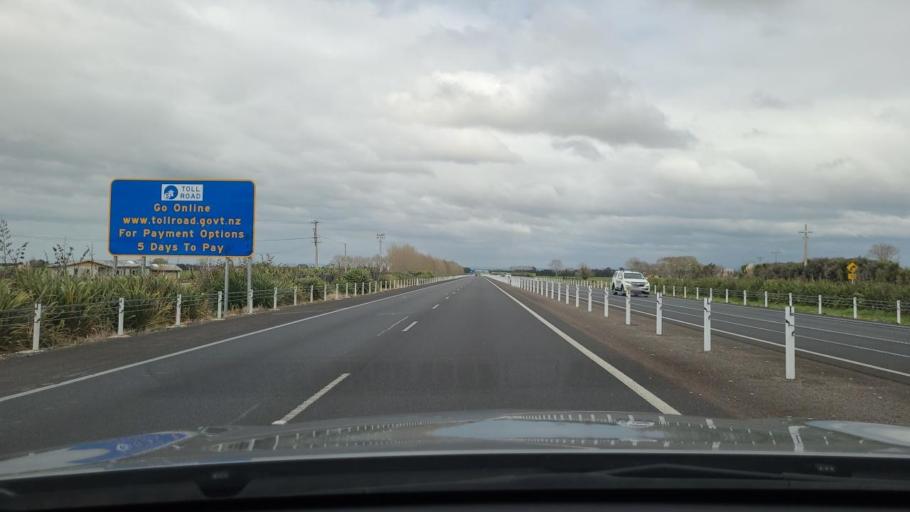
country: NZ
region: Bay of Plenty
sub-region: Western Bay of Plenty District
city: Maketu
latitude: -37.7633
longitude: 176.3712
